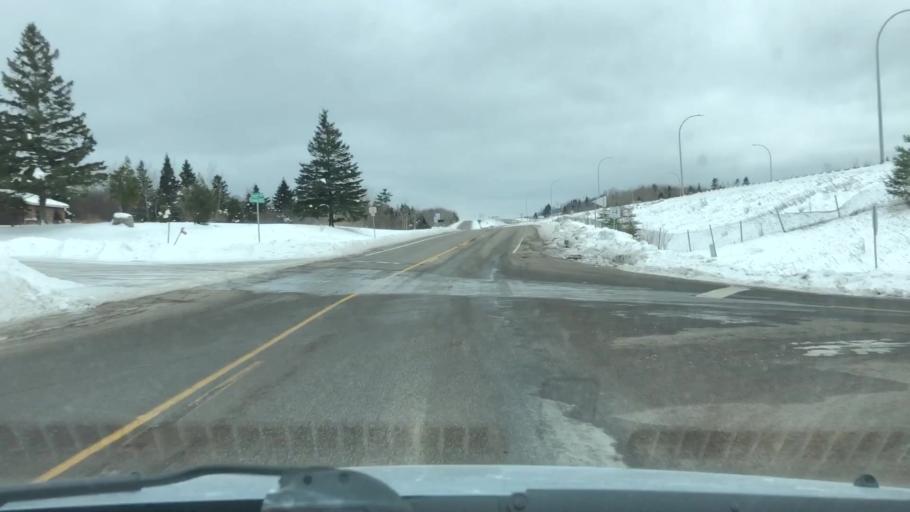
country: US
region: Minnesota
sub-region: Saint Louis County
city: Proctor
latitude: 46.7210
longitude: -92.2379
